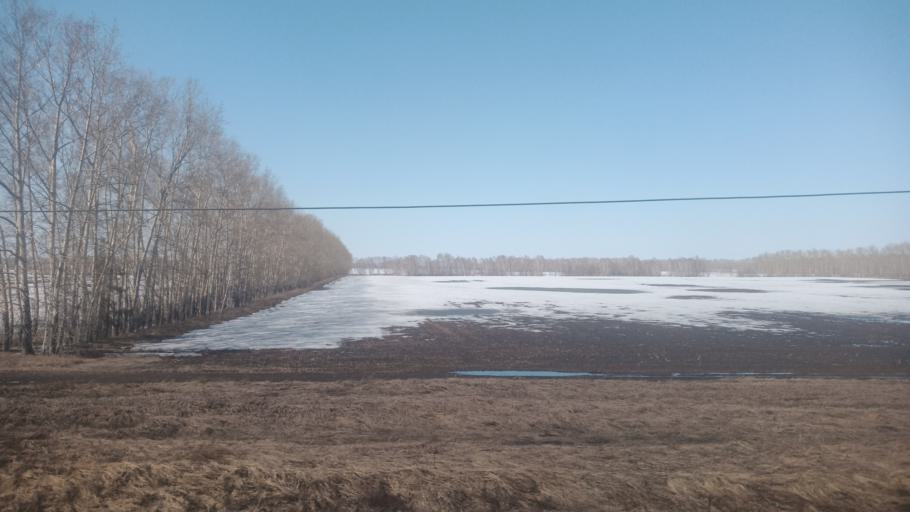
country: RU
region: Altai Krai
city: Logovskoye
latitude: 53.4856
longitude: 84.1542
